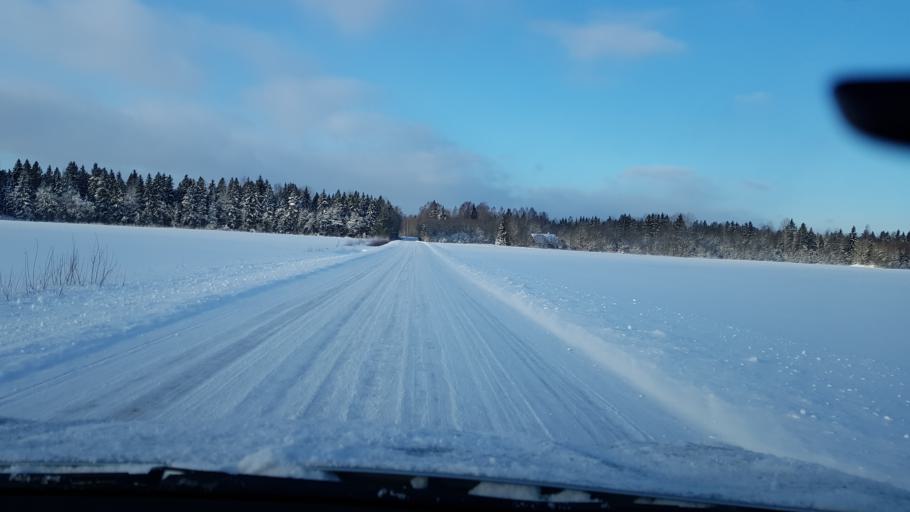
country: EE
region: Harju
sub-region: Nissi vald
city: Turba
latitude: 59.1020
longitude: 24.2477
